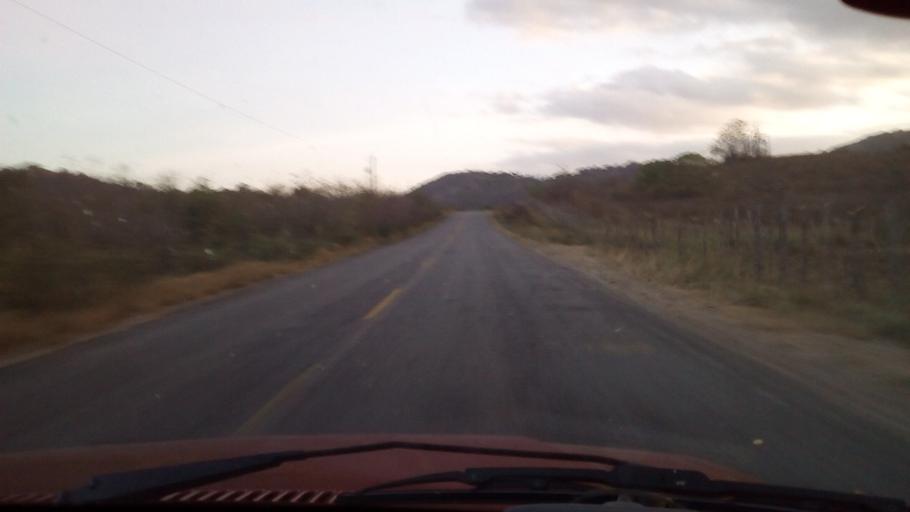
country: BR
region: Paraiba
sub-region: Bananeiras
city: Solanea
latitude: -6.7268
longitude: -35.5370
